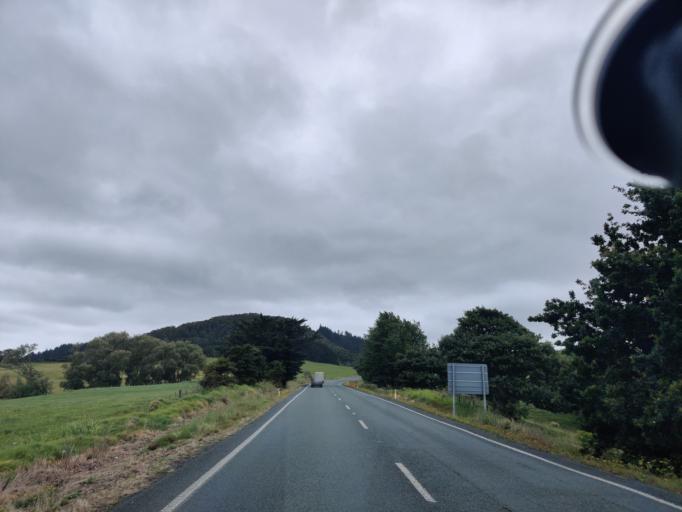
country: NZ
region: Northland
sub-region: Whangarei
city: Ruakaka
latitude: -36.0986
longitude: 174.4223
